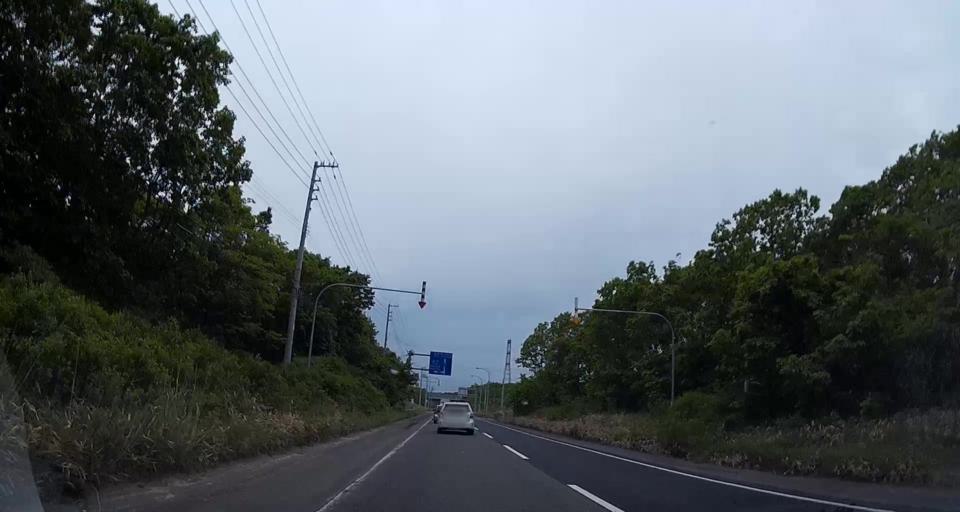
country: JP
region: Hokkaido
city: Chitose
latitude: 42.7120
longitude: 141.7498
